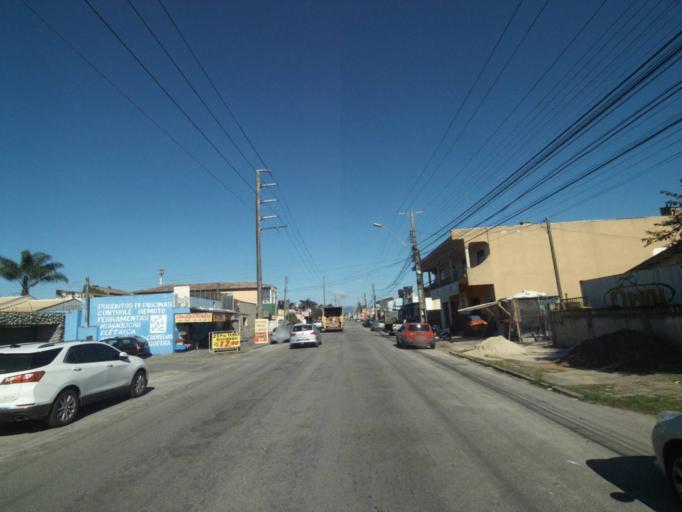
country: BR
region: Parana
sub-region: Paranagua
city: Paranagua
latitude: -25.5195
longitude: -48.5178
